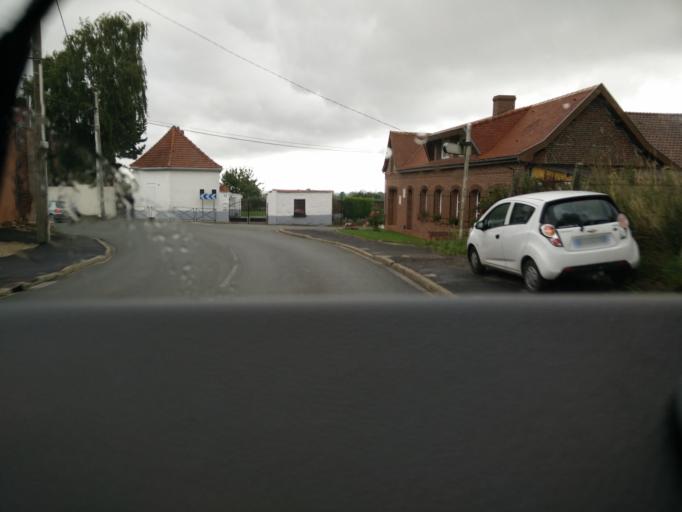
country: FR
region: Nord-Pas-de-Calais
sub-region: Departement du Pas-de-Calais
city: Bouvigny-Boyeffles
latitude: 50.4329
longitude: 2.6747
